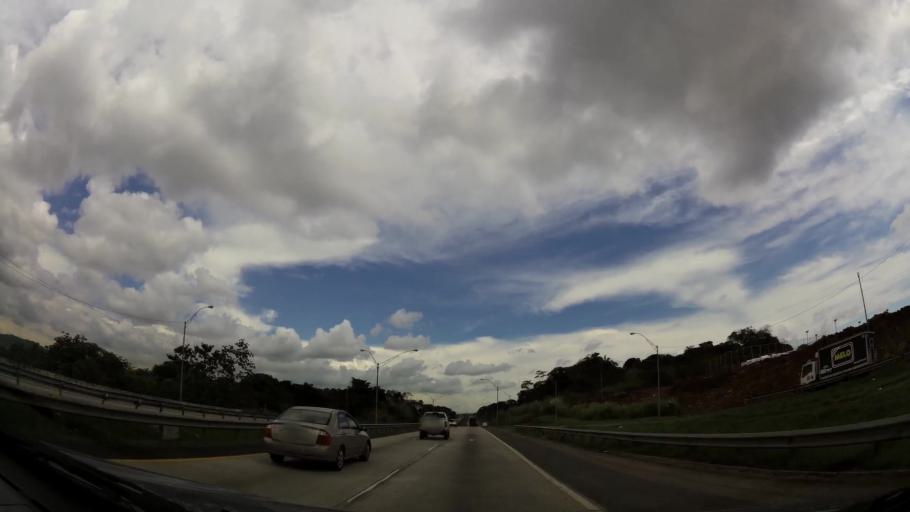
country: PA
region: Panama
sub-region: Distrito Arraijan
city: Arraijan
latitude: 8.9613
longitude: -79.6558
